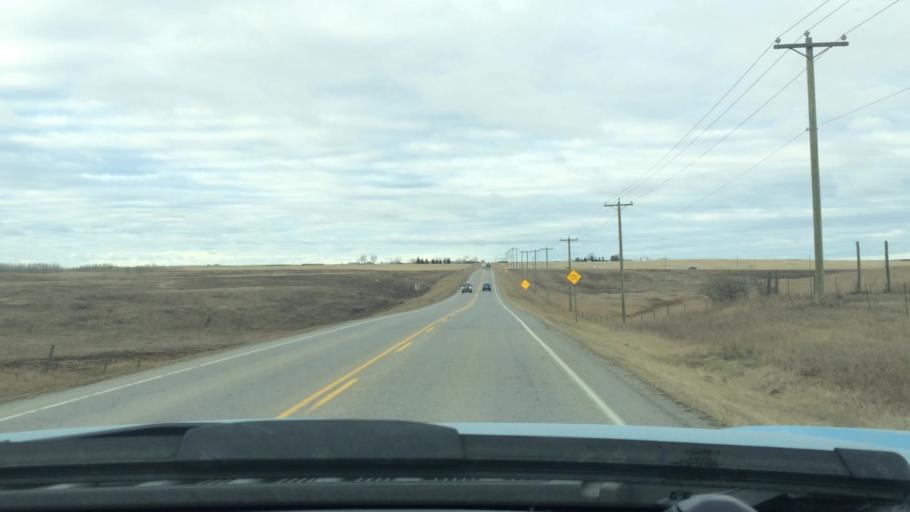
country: CA
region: Alberta
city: Airdrie
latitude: 51.2126
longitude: -114.0164
